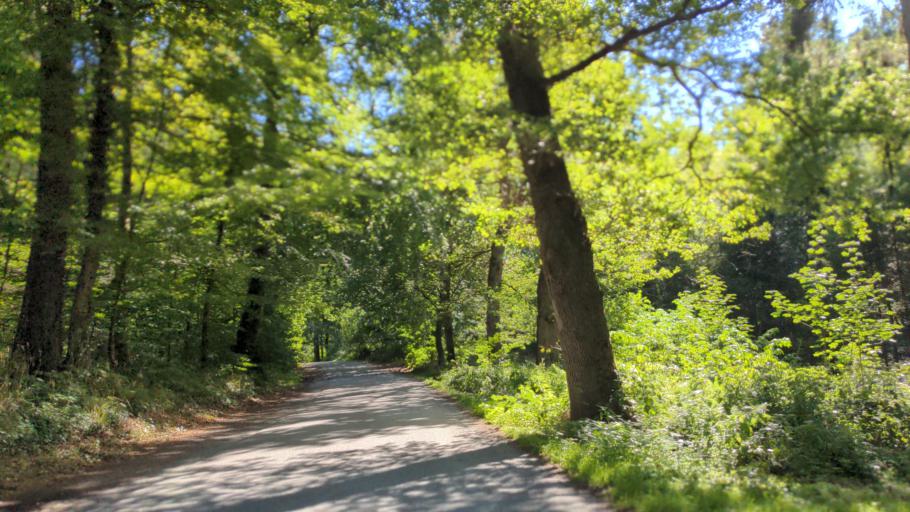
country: DE
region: Schleswig-Holstein
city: Kasseedorf
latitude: 54.1487
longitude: 10.7239
